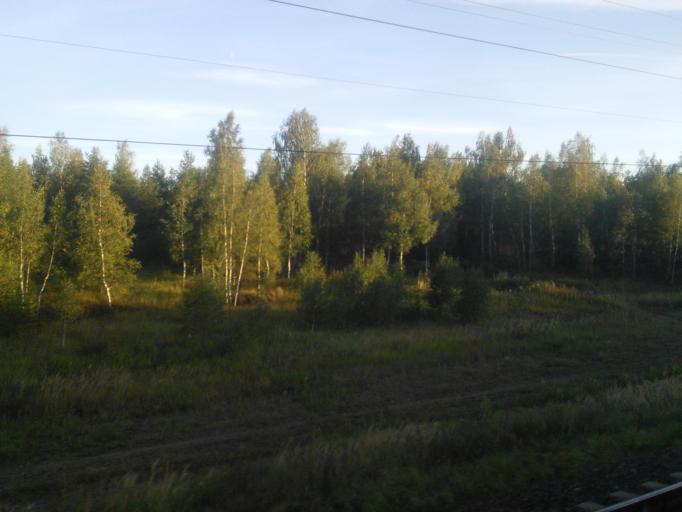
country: RU
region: Moskovskaya
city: Fryazevo
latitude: 55.7455
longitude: 38.5235
